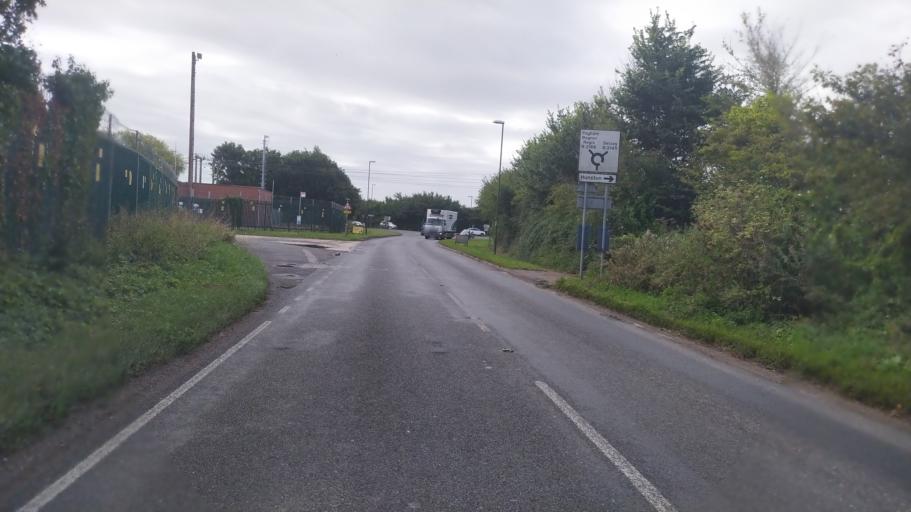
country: GB
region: England
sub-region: West Sussex
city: Chichester
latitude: 50.8171
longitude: -0.7682
